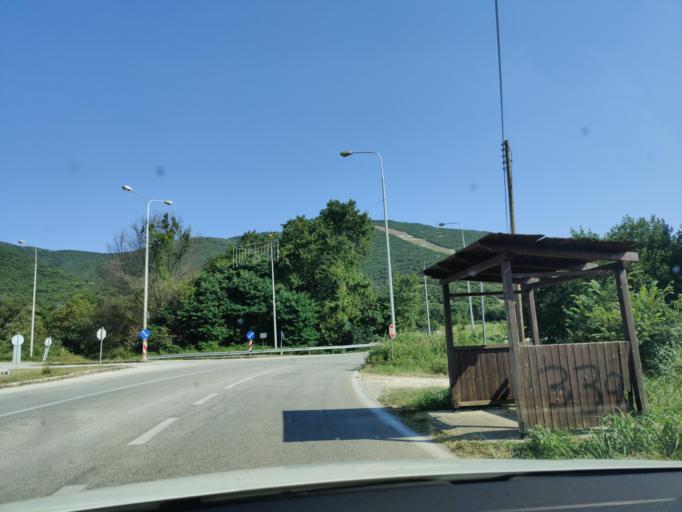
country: GR
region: East Macedonia and Thrace
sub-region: Nomos Kavalas
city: Zygos
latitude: 40.9967
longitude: 24.3830
